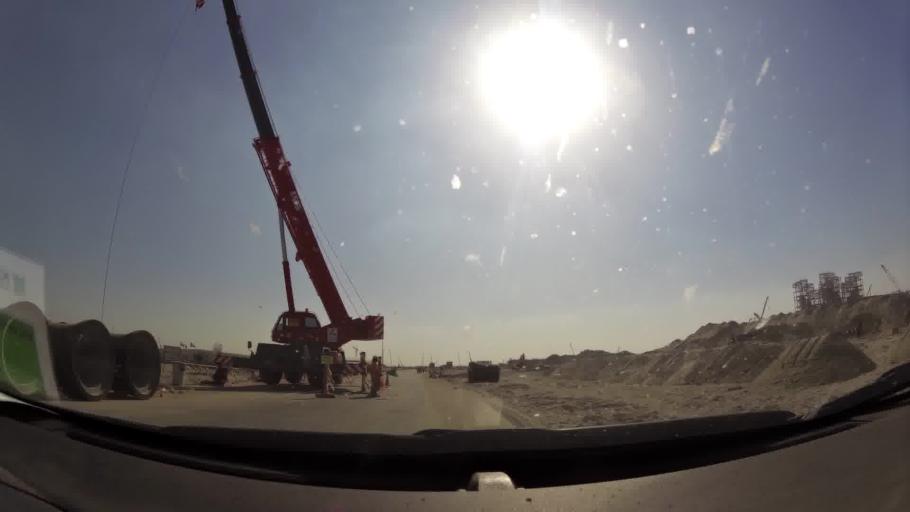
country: SA
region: Eastern Province
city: Al Khafji
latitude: 28.7094
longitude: 48.3404
